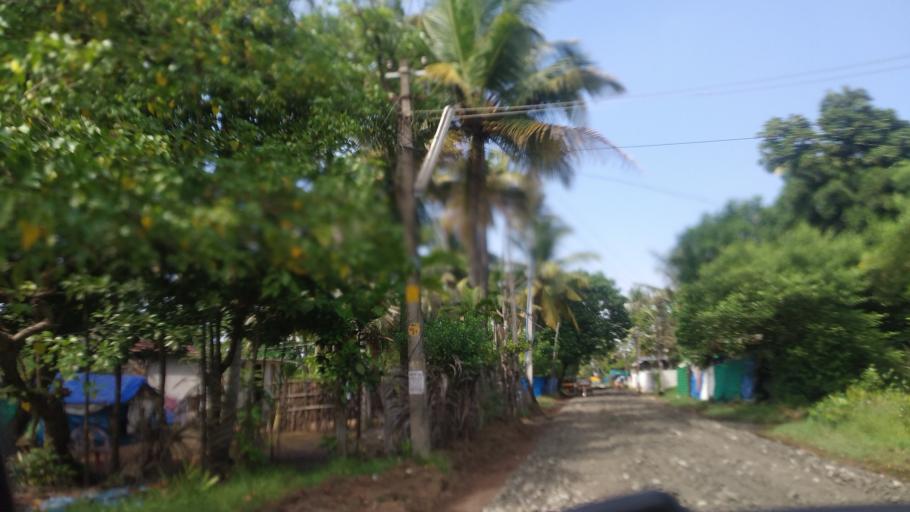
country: IN
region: Kerala
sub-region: Ernakulam
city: Elur
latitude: 10.0561
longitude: 76.2018
